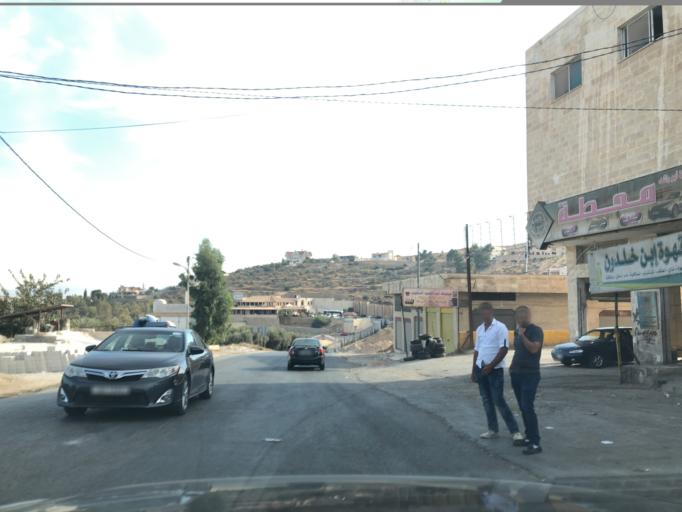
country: JO
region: Jerash
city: Jarash
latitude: 32.2694
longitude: 35.8872
